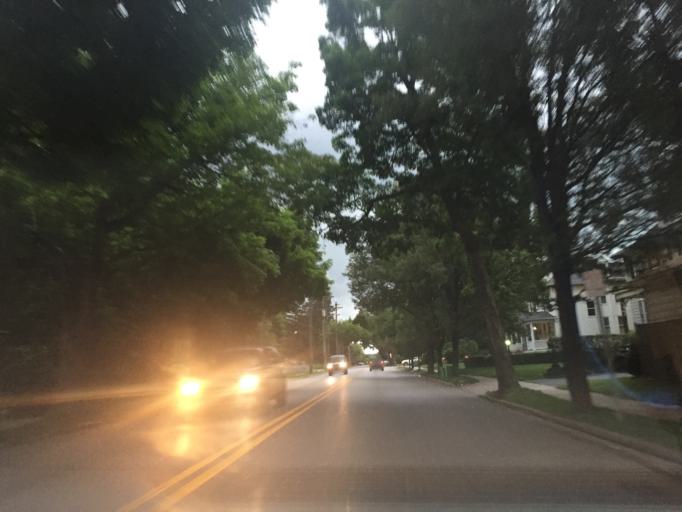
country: US
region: Pennsylvania
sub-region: York County
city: West York
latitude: 39.9647
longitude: -76.7451
